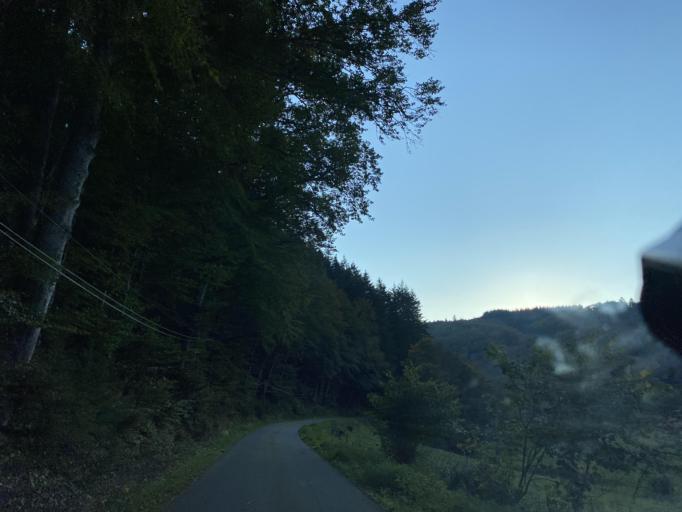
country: FR
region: Rhone-Alpes
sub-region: Departement de la Loire
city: Saint-Just-en-Chevalet
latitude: 45.9510
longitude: 3.8603
